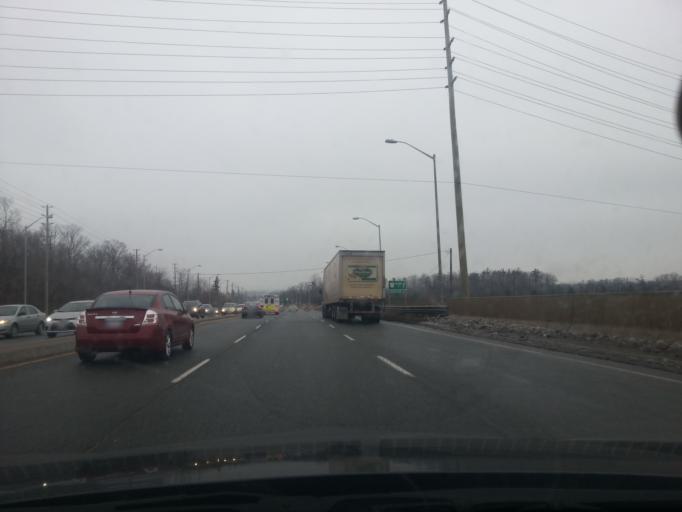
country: CA
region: Ontario
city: Concord
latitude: 43.8291
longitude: -79.4541
